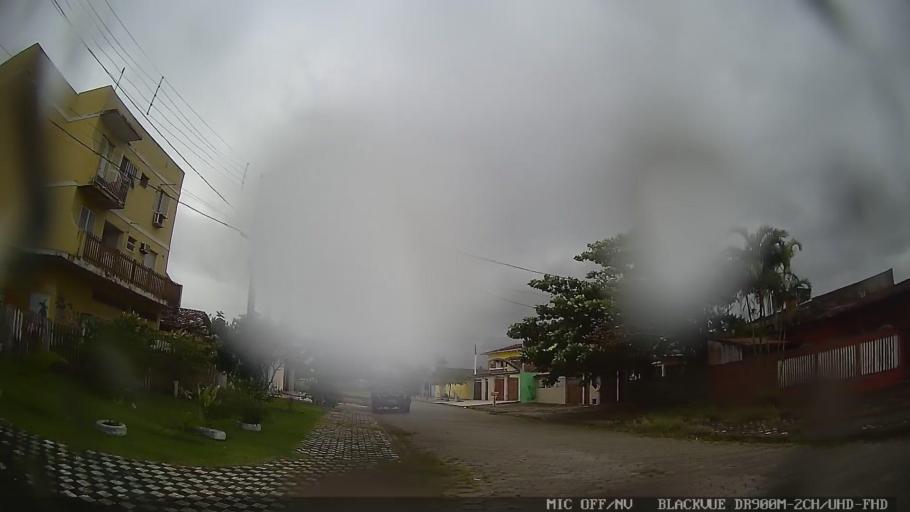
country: BR
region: Sao Paulo
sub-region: Mongagua
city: Mongagua
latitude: -24.1321
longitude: -46.6922
